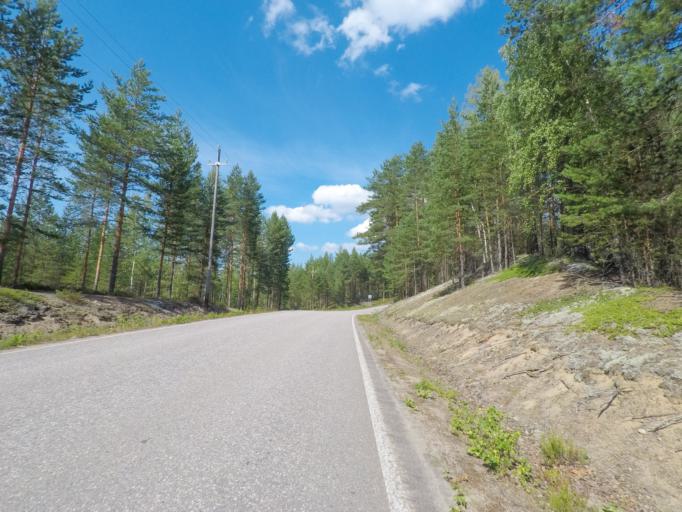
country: FI
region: Southern Savonia
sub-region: Mikkeli
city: Puumala
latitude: 61.4590
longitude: 28.1750
